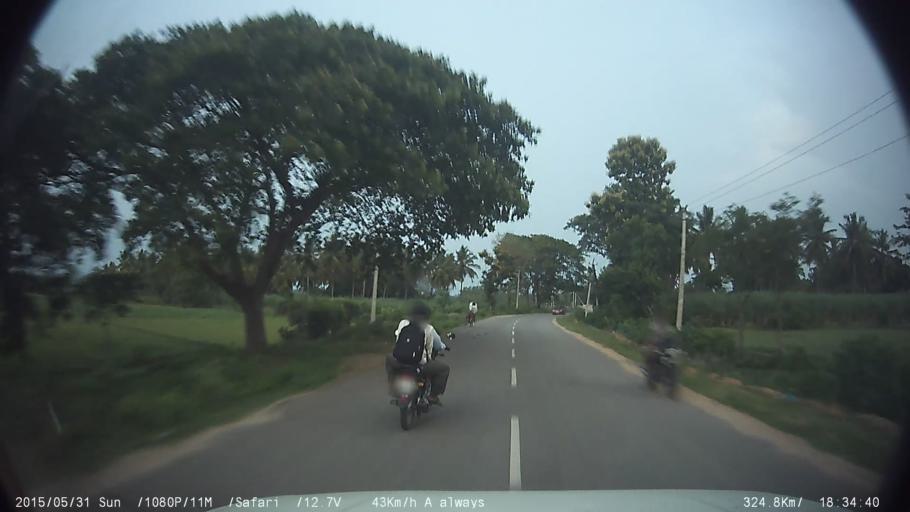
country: IN
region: Karnataka
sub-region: Mysore
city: Nanjangud
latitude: 12.1444
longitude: 76.7573
